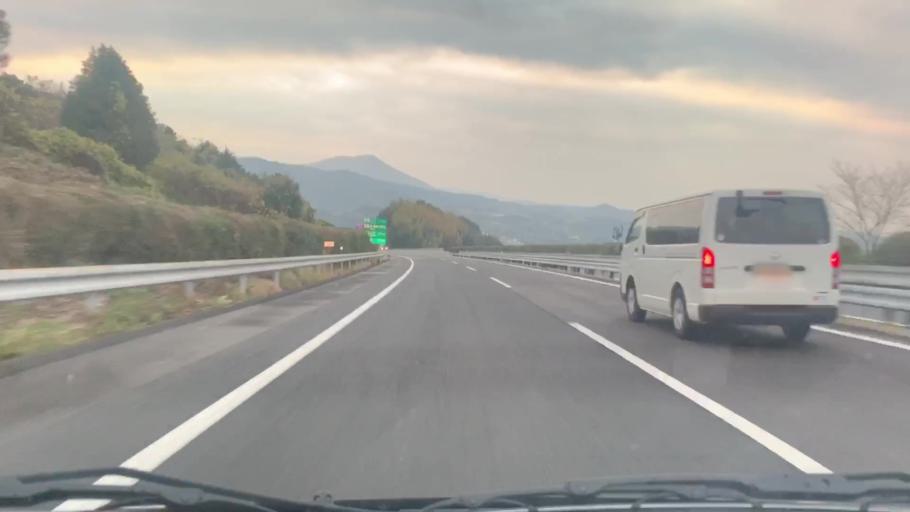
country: JP
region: Nagasaki
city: Omura
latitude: 33.0291
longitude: 129.9315
